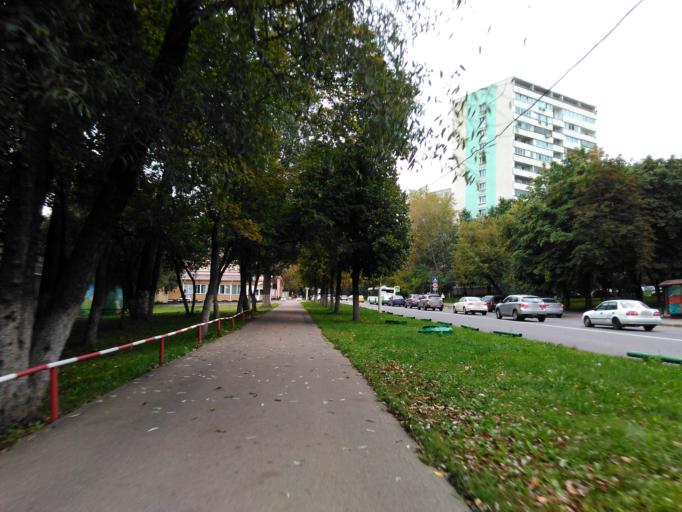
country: RU
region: Moscow
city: Zyuzino
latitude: 55.6634
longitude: 37.5805
